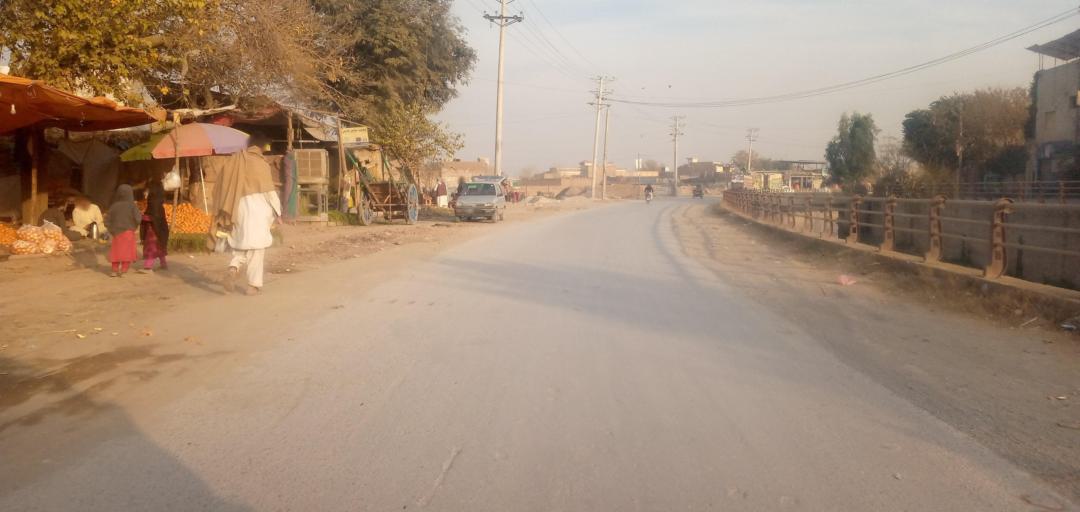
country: PK
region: Khyber Pakhtunkhwa
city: Peshawar
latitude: 33.9740
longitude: 71.5276
